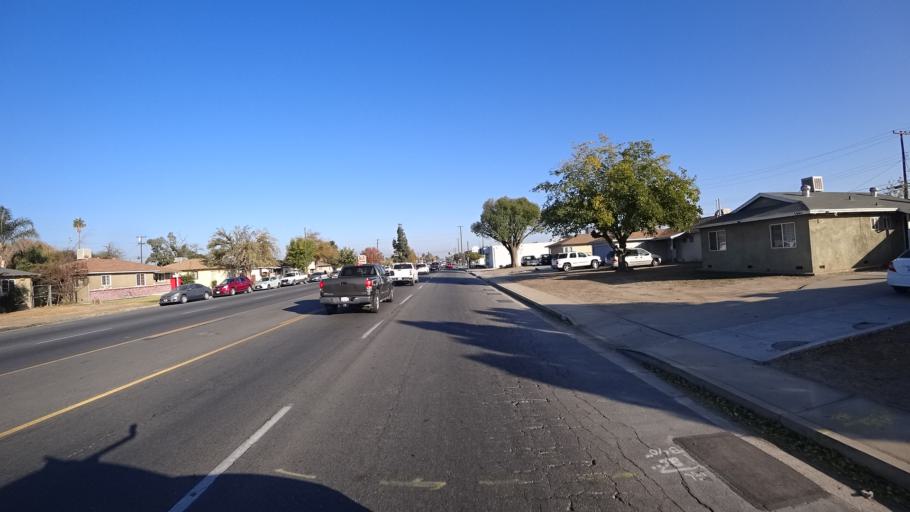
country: US
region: California
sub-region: Kern County
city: Bakersfield
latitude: 35.3394
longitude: -119.0230
